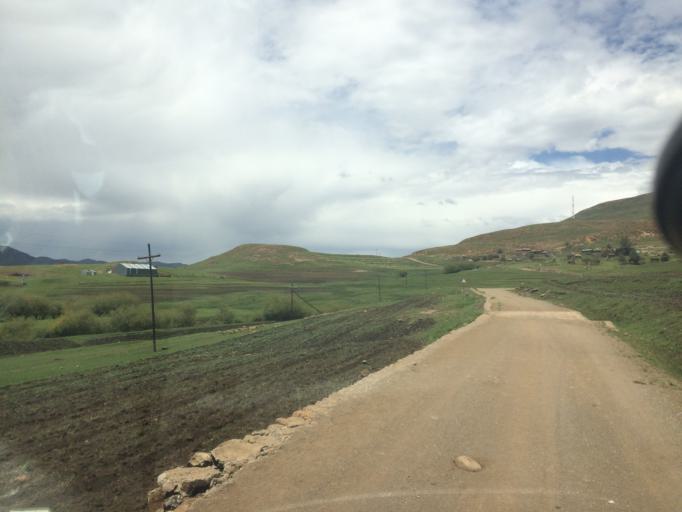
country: LS
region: Maseru
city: Nako
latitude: -29.8620
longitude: 28.0382
